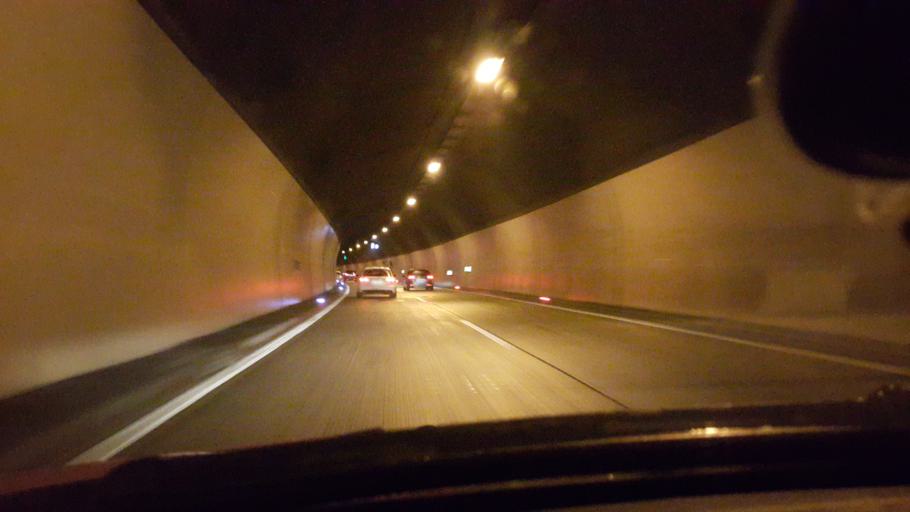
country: SI
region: Slovenska Konjice
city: Slovenske Konjice
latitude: 46.2971
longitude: 15.4414
